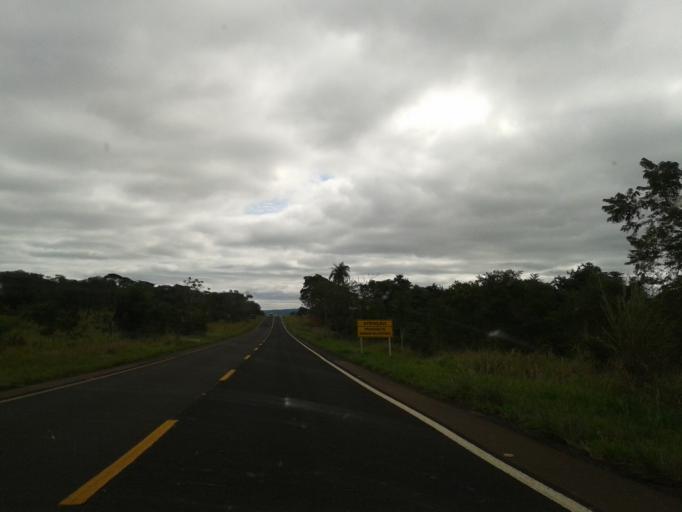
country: BR
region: Minas Gerais
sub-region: Campina Verde
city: Campina Verde
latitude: -19.5201
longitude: -49.6355
